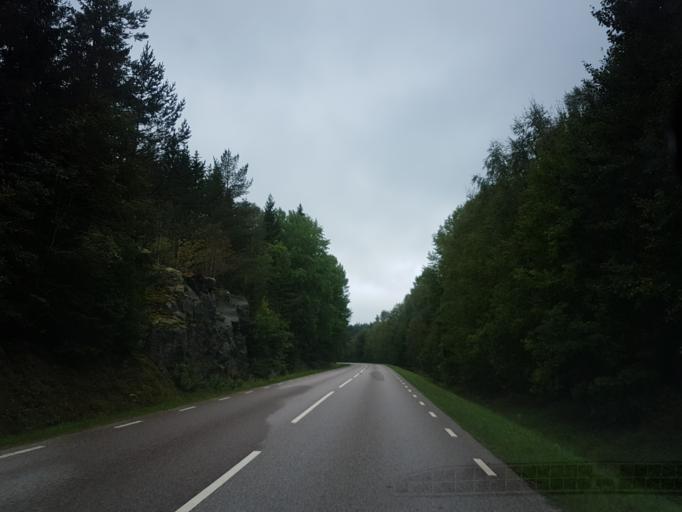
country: SE
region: OEstergoetland
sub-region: Atvidabergs Kommun
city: Atvidaberg
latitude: 58.2310
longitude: 16.0033
